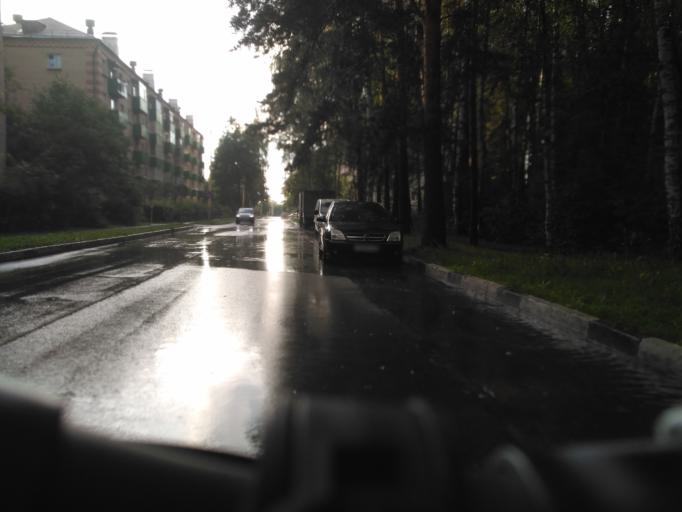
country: RU
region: Moskovskaya
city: Dubna
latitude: 56.7538
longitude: 37.2014
